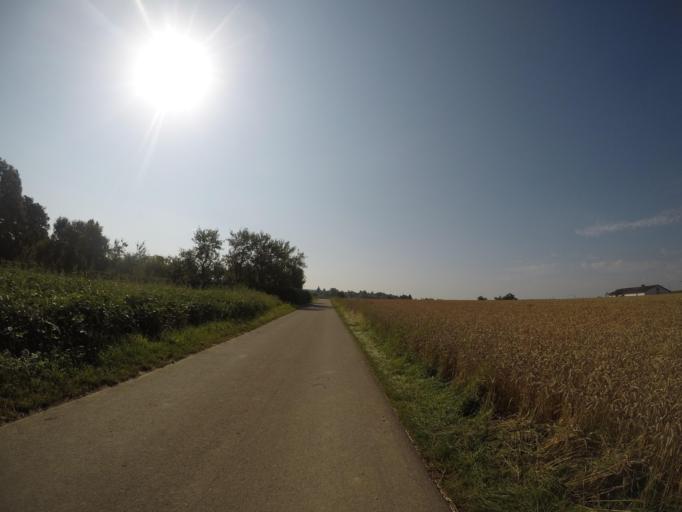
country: DE
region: Baden-Wuerttemberg
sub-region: Tuebingen Region
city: Wain
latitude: 48.1984
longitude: 10.0174
